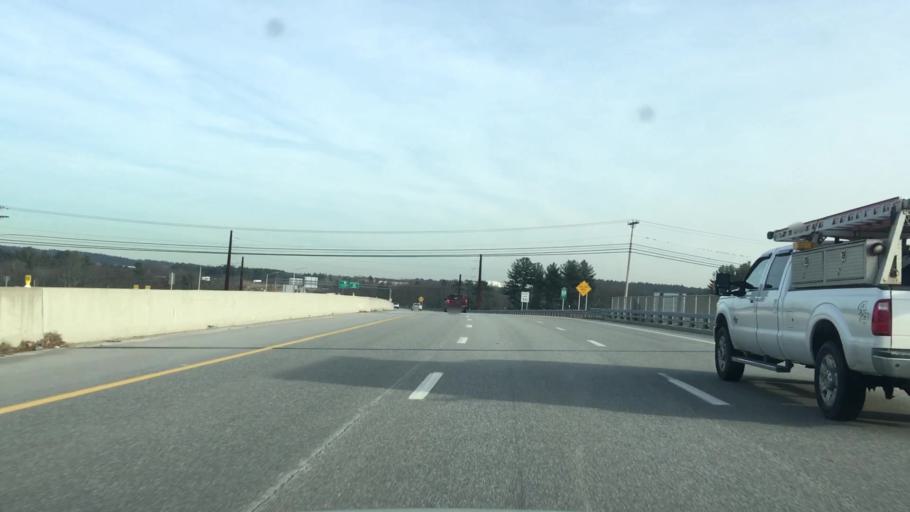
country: US
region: New Hampshire
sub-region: Hillsborough County
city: East Merrimack
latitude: 42.9127
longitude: -71.4596
